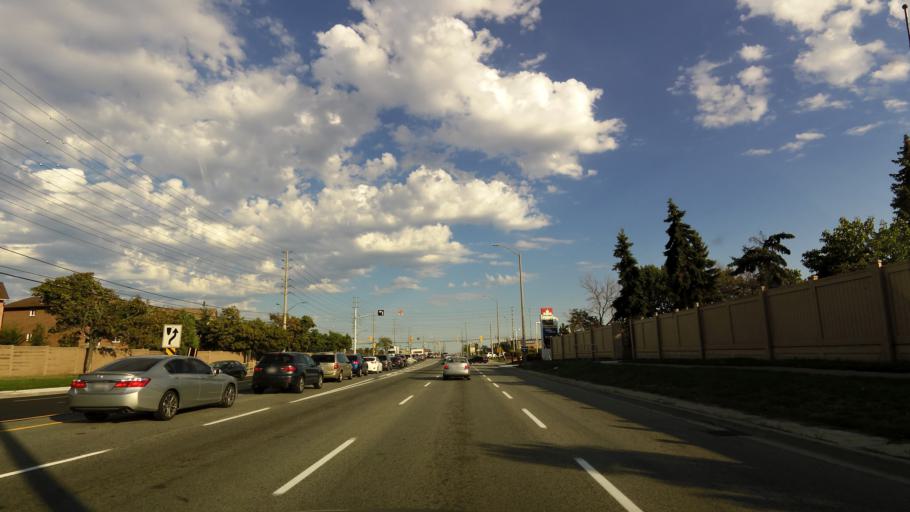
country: CA
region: Ontario
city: Mississauga
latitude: 43.5803
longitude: -79.6530
